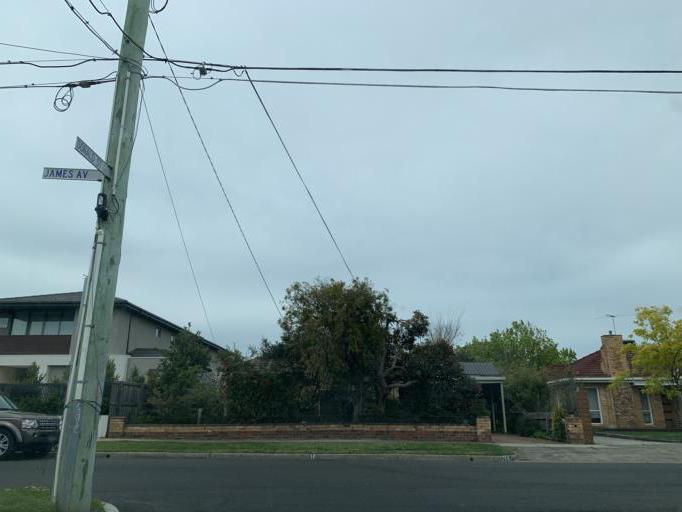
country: AU
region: Victoria
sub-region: Bayside
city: Highett
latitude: -37.9523
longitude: 145.0379
